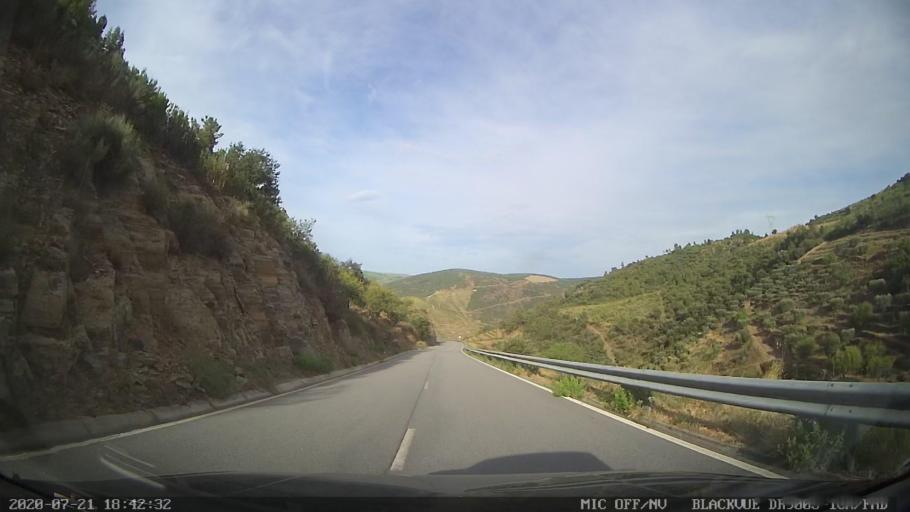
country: PT
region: Viseu
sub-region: Sao Joao da Pesqueira
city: Sao Joao da Pesqueira
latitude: 41.1103
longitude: -7.4674
